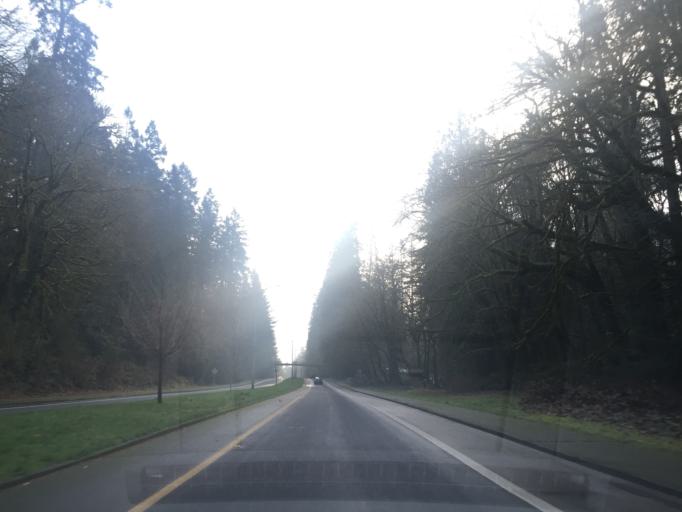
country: US
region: Washington
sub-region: Thurston County
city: Olympia
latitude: 47.0723
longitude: -122.8948
